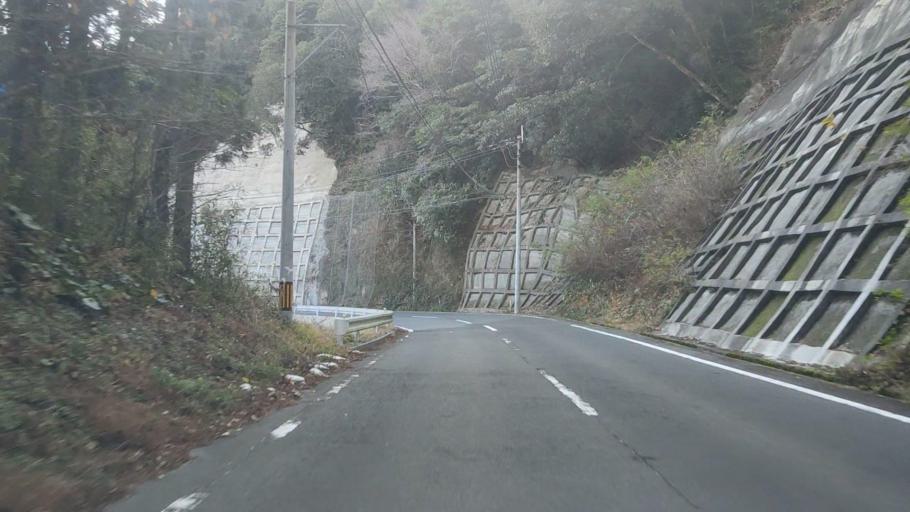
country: JP
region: Kagoshima
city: Kokubu-matsuki
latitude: 31.6690
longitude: 130.8376
